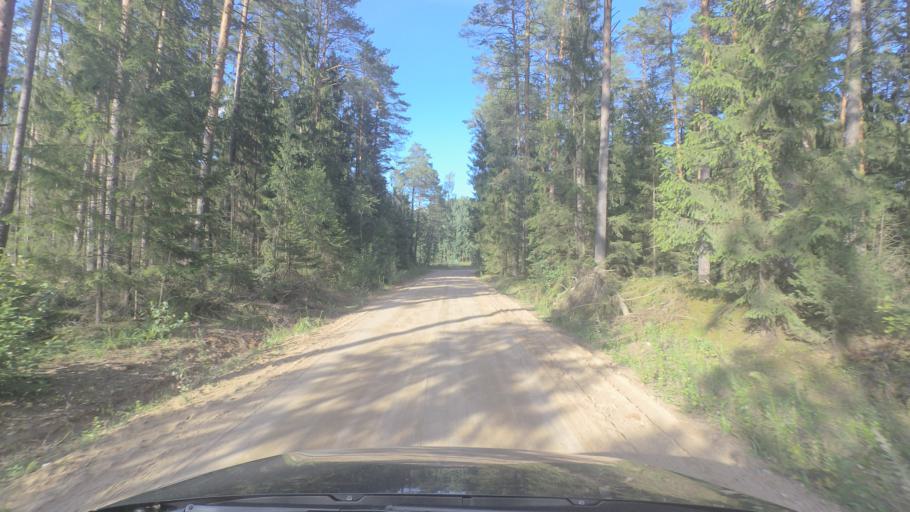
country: LT
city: Svencioneliai
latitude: 55.1660
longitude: 25.8341
